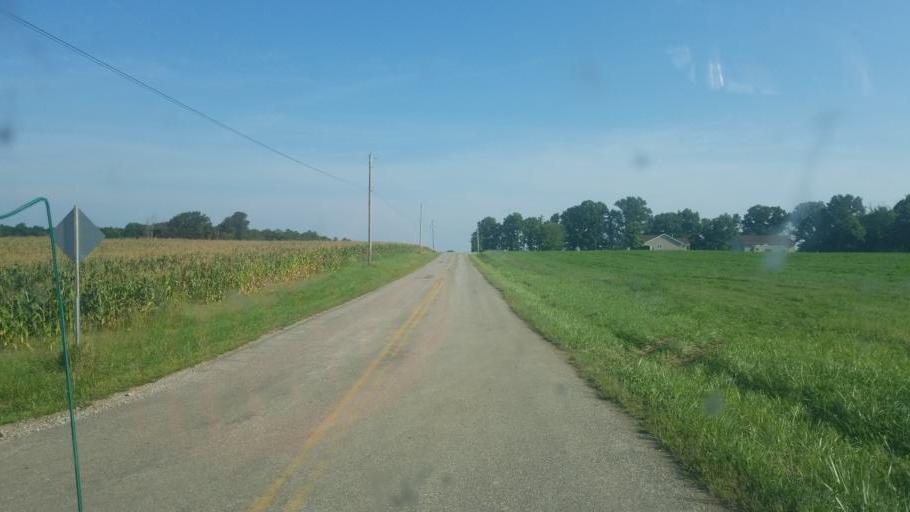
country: US
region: Ohio
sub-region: Huron County
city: New London
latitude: 41.0510
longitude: -82.3576
